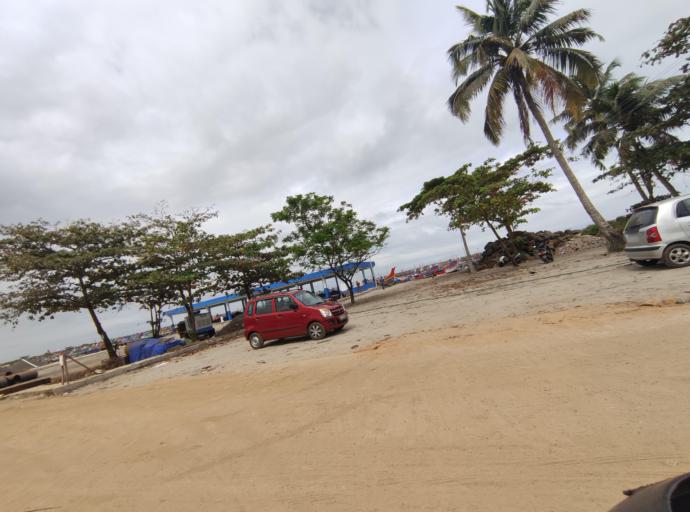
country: IN
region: Kerala
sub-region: Alappuzha
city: Kutiatodu
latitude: 9.8010
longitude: 76.2754
